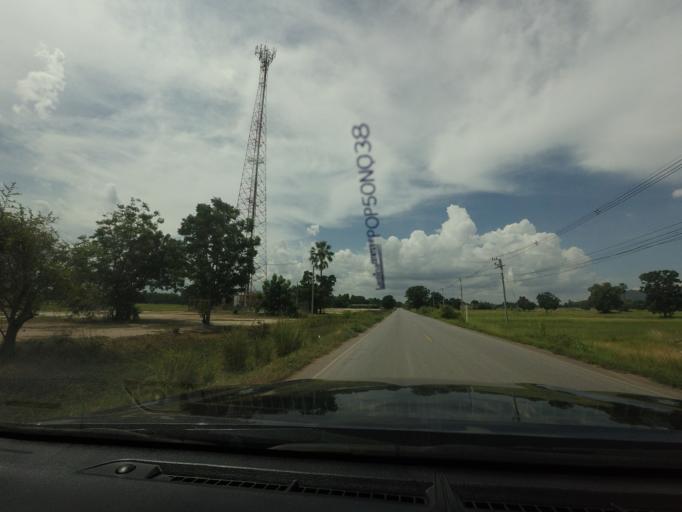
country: TH
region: Kanchanaburi
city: Phanom Thuan
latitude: 14.1561
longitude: 99.6178
